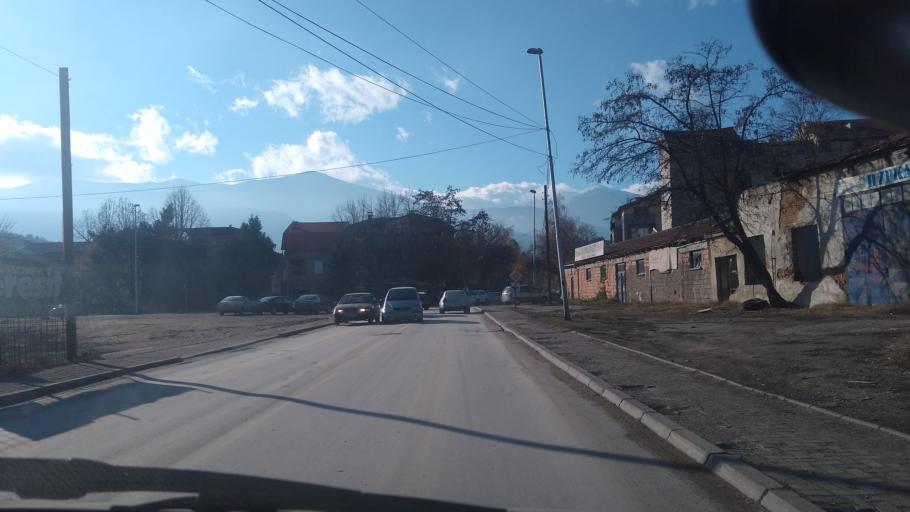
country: MK
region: Bitola
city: Bitola
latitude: 41.0240
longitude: 21.3426
